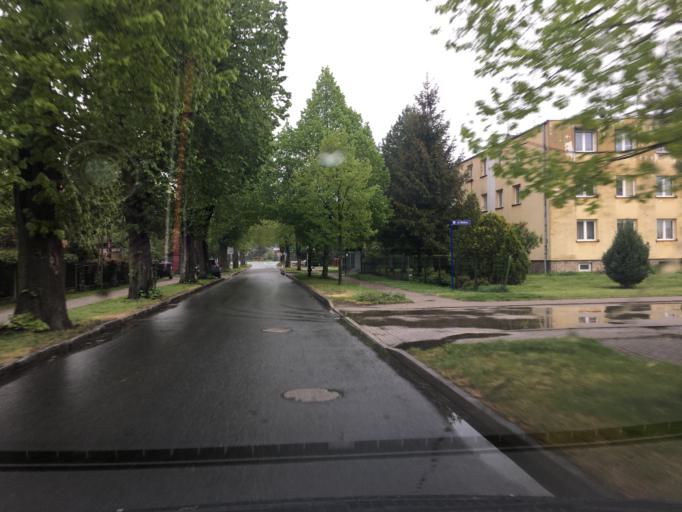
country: PL
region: Lower Silesian Voivodeship
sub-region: Powiat wroclawski
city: Zerniki Wroclawskie
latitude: 51.0308
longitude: 17.0625
